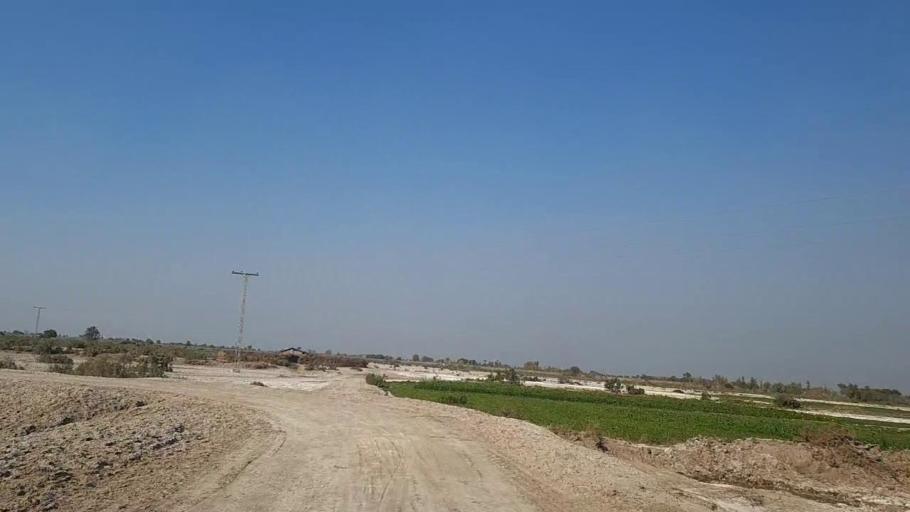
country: PK
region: Sindh
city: Daur
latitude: 26.3198
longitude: 68.1912
